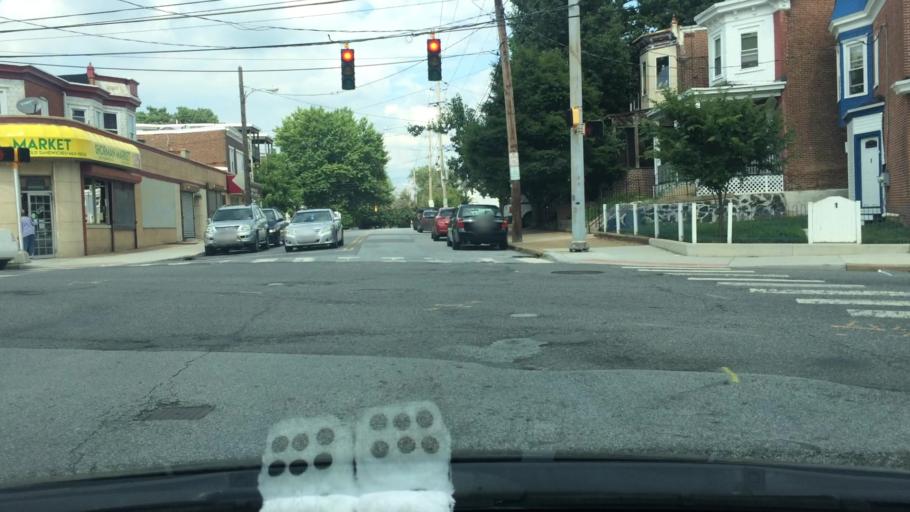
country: US
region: Delaware
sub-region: New Castle County
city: Wilmington
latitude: 39.7557
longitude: -75.5416
